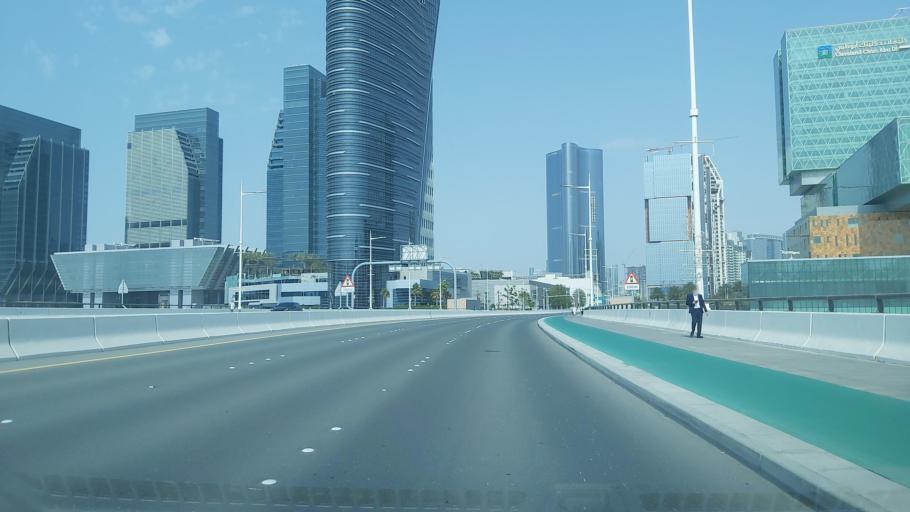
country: AE
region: Abu Dhabi
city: Abu Dhabi
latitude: 24.4990
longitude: 54.3847
